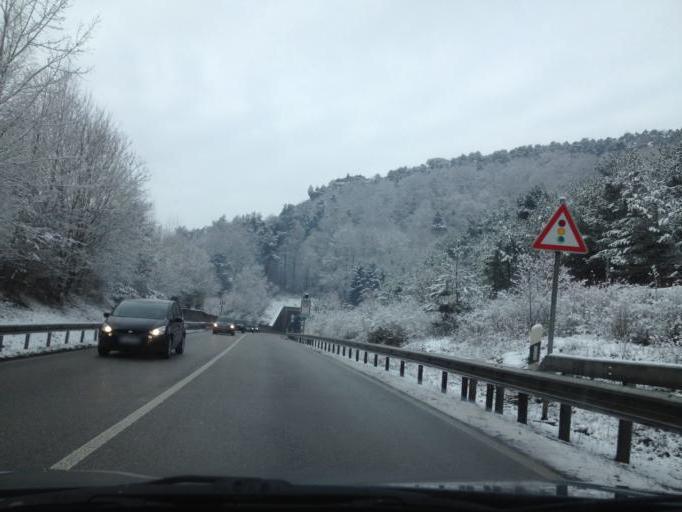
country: DE
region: Rheinland-Pfalz
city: Rinnthal
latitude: 49.2196
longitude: 7.9278
